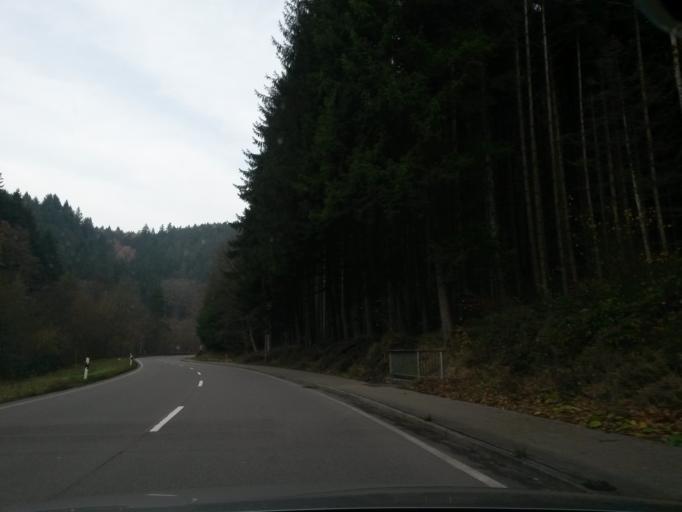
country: DE
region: Baden-Wuerttemberg
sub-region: Karlsruhe Region
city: Alpirsbach
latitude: 48.3242
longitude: 8.3955
